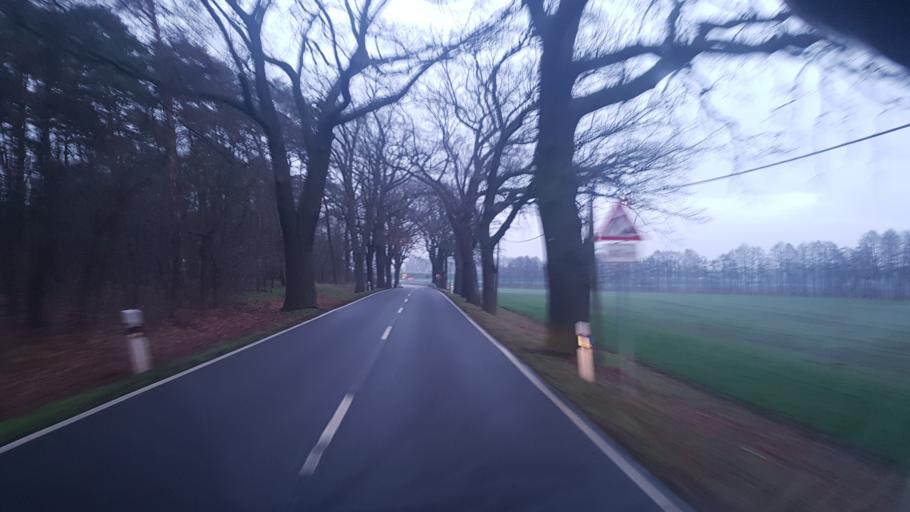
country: DE
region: Brandenburg
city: Trebbin
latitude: 52.2405
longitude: 13.2232
